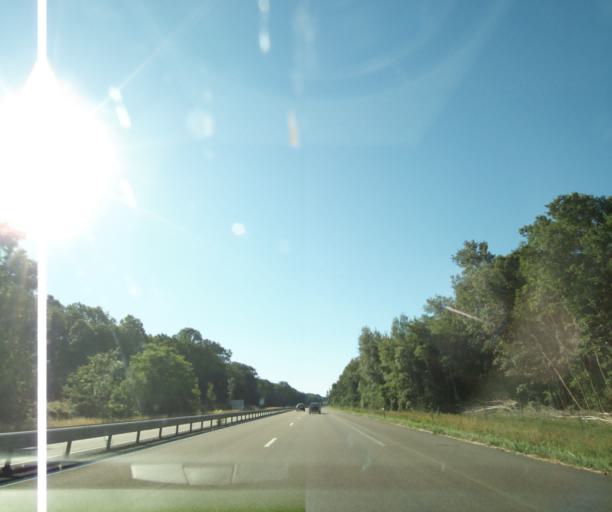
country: FR
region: Champagne-Ardenne
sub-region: Departement de l'Aube
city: Lusigny-sur-Barse
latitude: 48.1967
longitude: 4.2662
